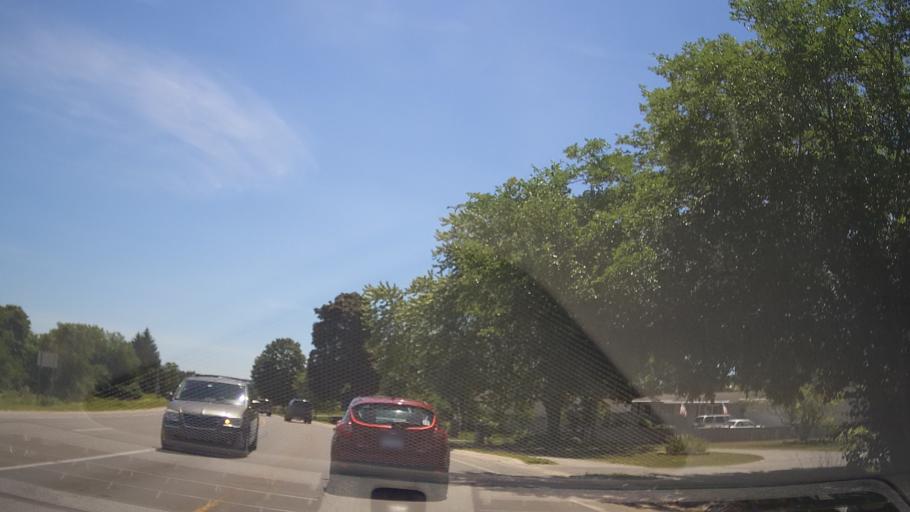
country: US
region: Michigan
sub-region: Grand Traverse County
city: Traverse City
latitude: 44.7426
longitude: -85.6556
